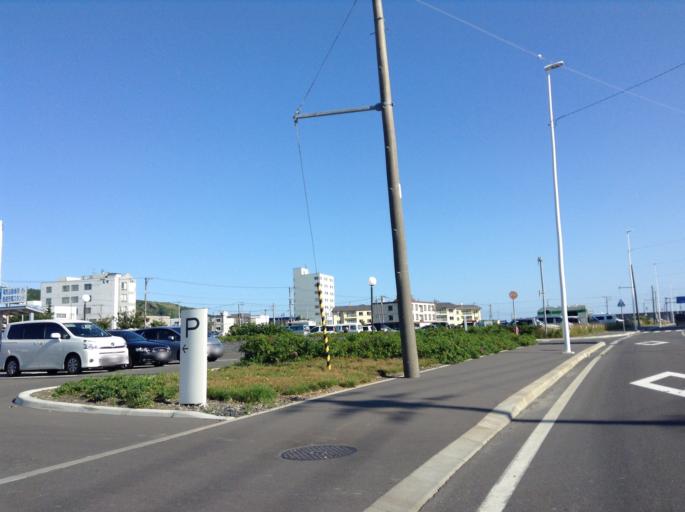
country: JP
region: Hokkaido
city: Wakkanai
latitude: 45.4182
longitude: 141.6779
